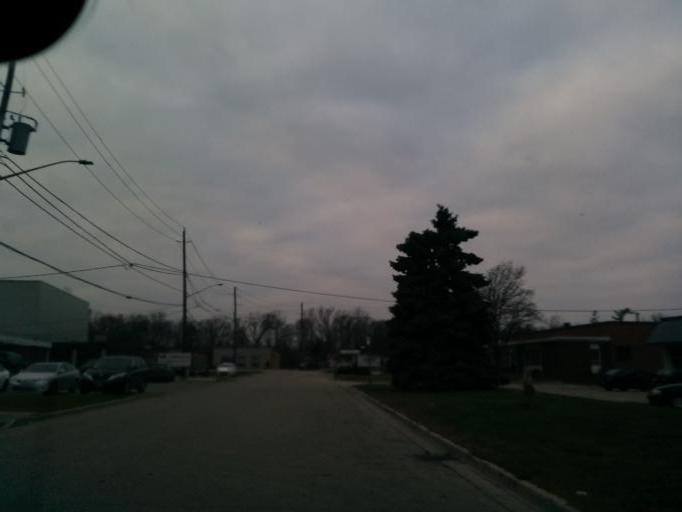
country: CA
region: Ontario
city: Etobicoke
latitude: 43.6144
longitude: -79.5818
